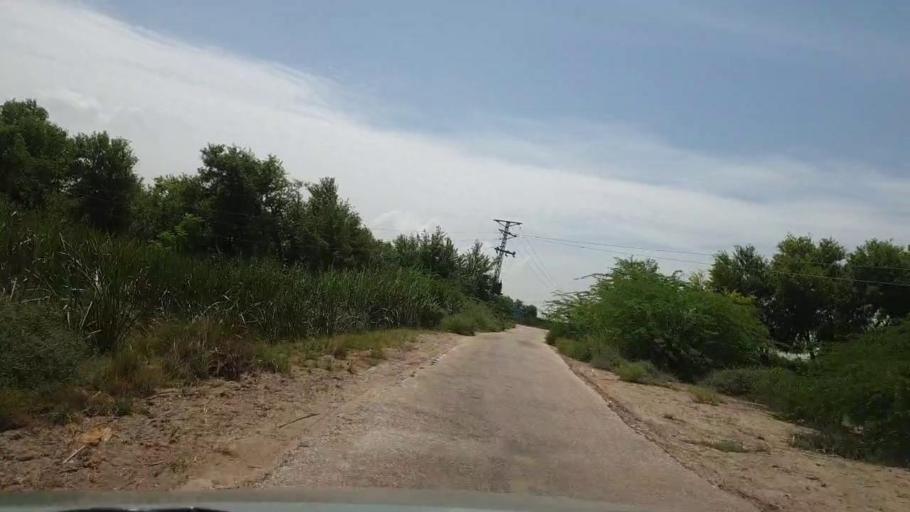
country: PK
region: Sindh
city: Bozdar
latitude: 27.0665
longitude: 68.9825
